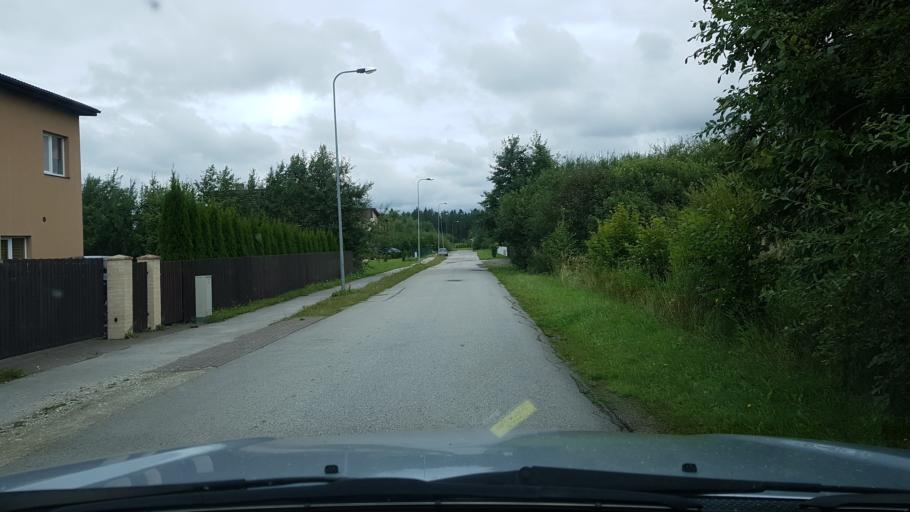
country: EE
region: Harju
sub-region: Rae vald
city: Vaida
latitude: 59.3172
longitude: 24.9488
